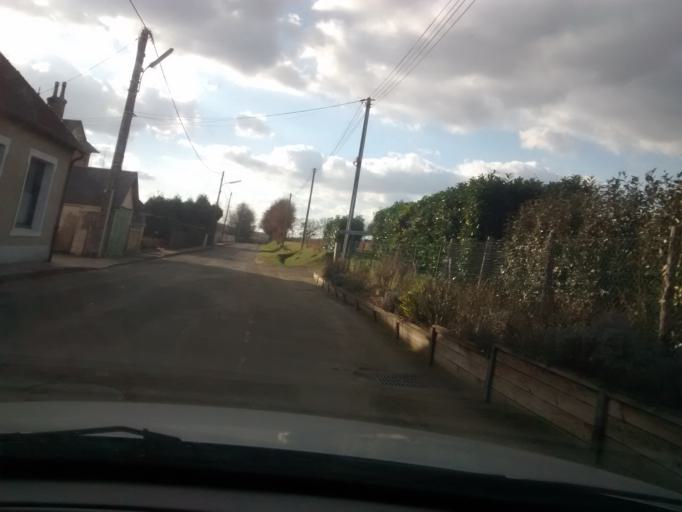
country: FR
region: Pays de la Loire
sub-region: Departement de la Sarthe
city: Le Breil-sur-Merize
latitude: 47.9749
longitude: 0.4587
